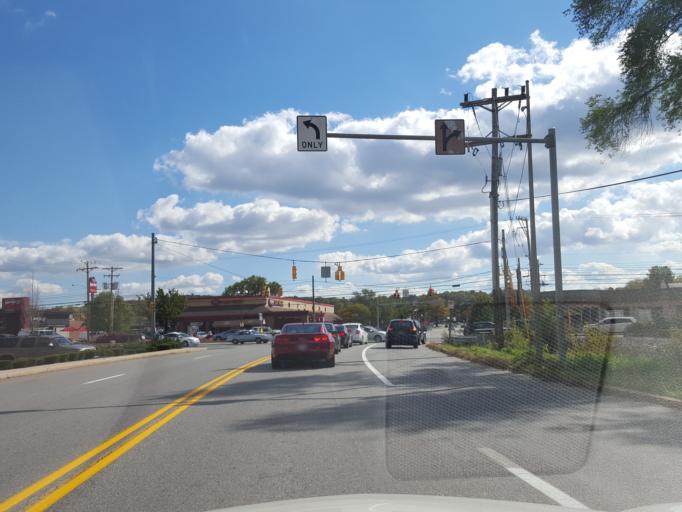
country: US
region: Pennsylvania
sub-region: York County
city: East York
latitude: 39.9758
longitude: -76.6736
